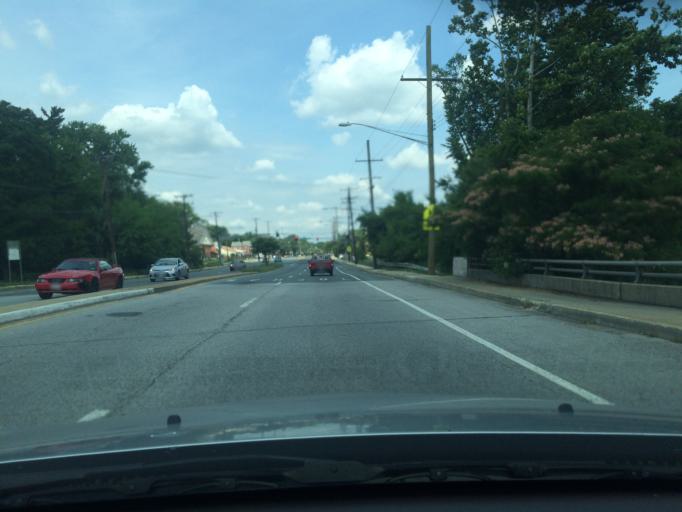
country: US
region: Maryland
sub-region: Prince George's County
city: Chillum
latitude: 38.9632
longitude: -76.9706
